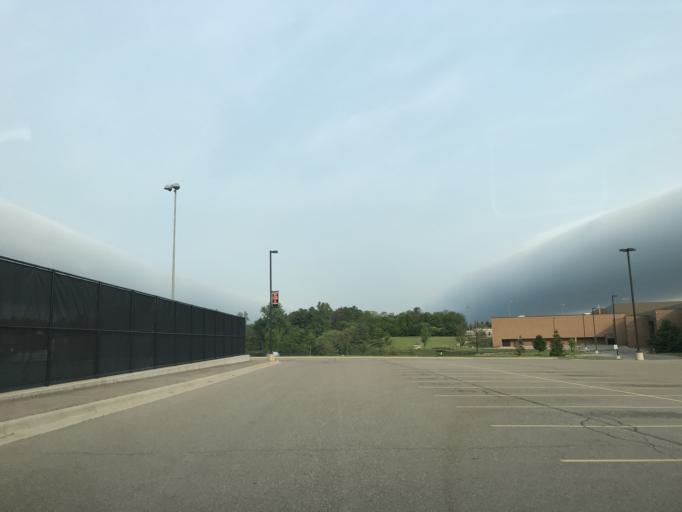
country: US
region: Michigan
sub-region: Livingston County
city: Brighton
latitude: 42.5248
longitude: -83.7934
